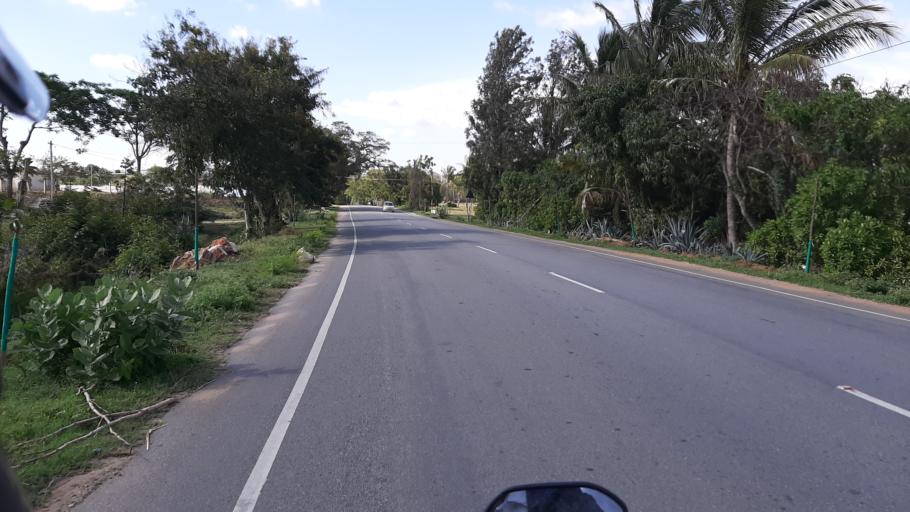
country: IN
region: Tamil Nadu
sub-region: Krishnagiri
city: Denkanikota
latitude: 12.5416
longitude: 77.7888
